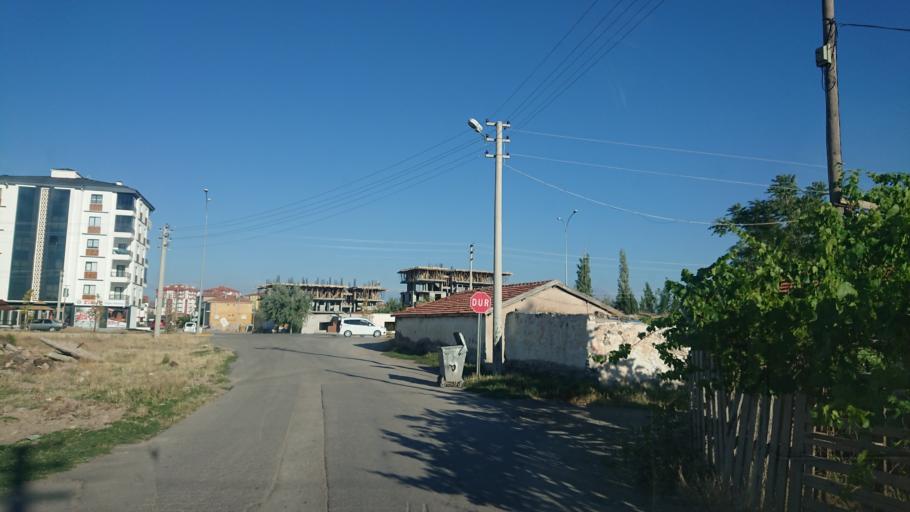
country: TR
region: Aksaray
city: Aksaray
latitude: 38.3824
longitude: 33.9914
